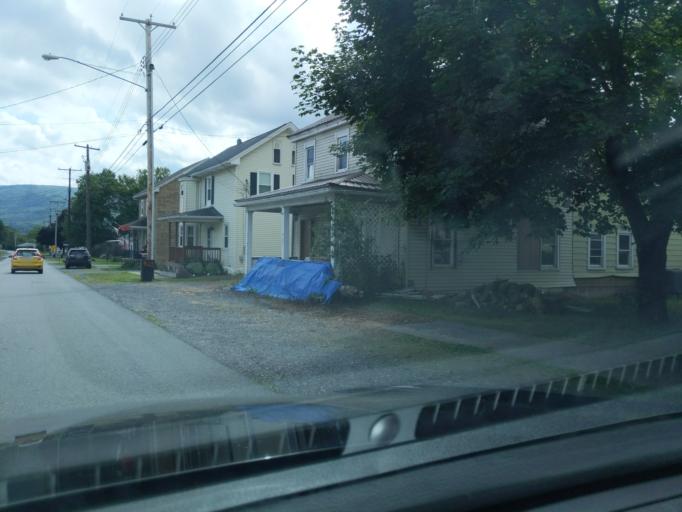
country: US
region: Pennsylvania
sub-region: Blair County
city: Duncansville
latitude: 40.3937
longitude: -78.4354
